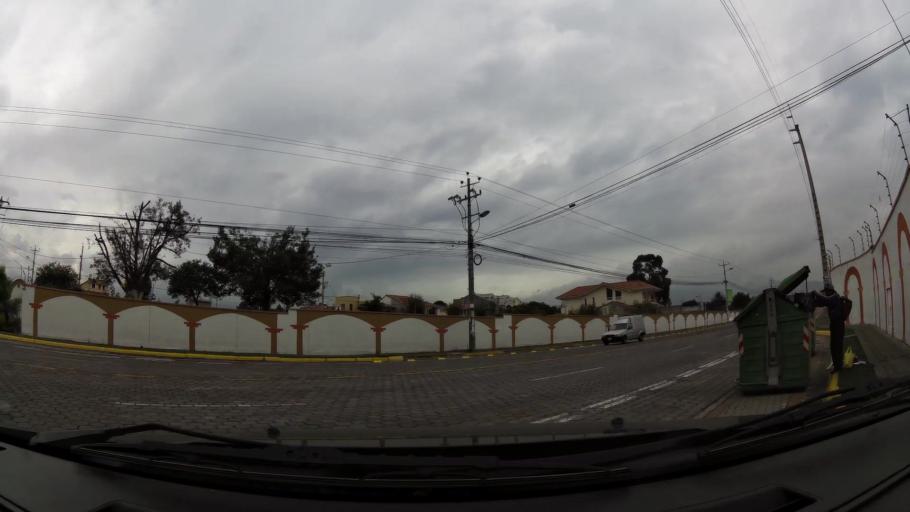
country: EC
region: Pichincha
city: Sangolqui
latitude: -0.3285
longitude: -78.4635
